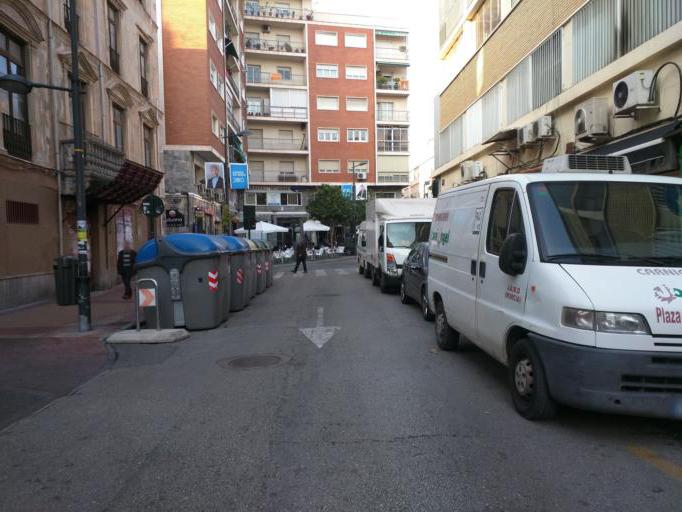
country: ES
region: Murcia
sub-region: Murcia
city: Murcia
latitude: 37.9867
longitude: -1.1273
